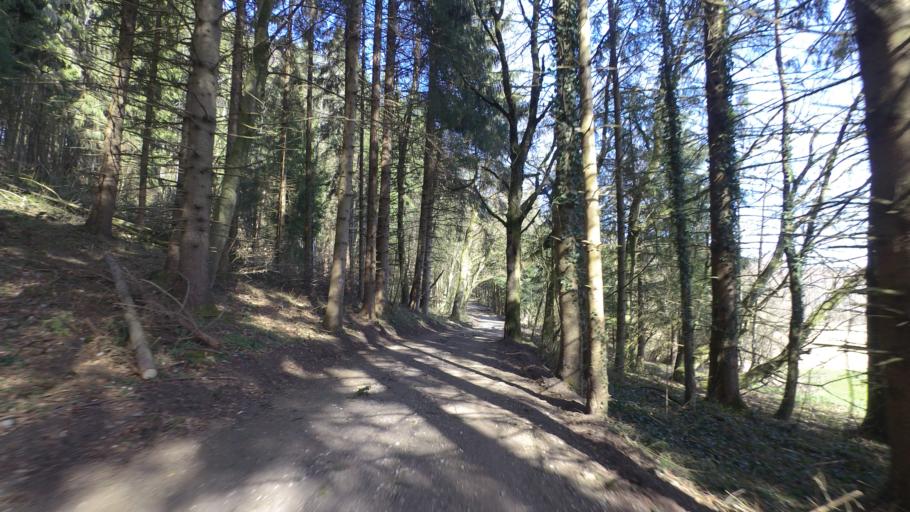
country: DE
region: Bavaria
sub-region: Upper Bavaria
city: Nussdorf
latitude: 47.9061
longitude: 12.5767
